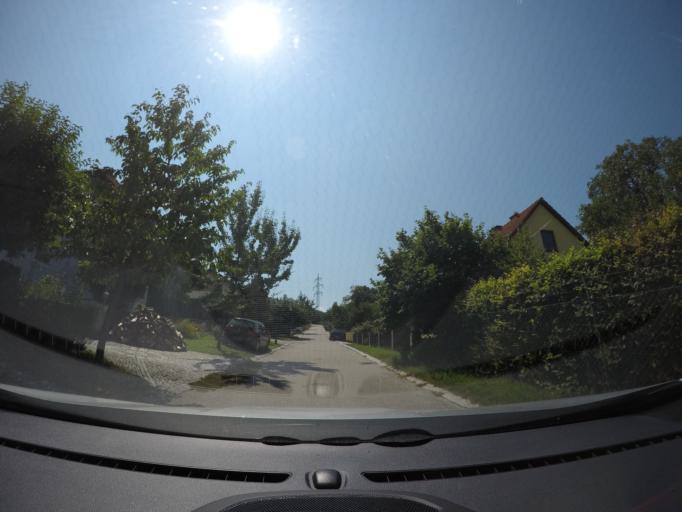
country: AT
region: Lower Austria
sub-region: Politischer Bezirk Sankt Polten
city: Asperhofen
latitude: 48.2190
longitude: 15.9307
